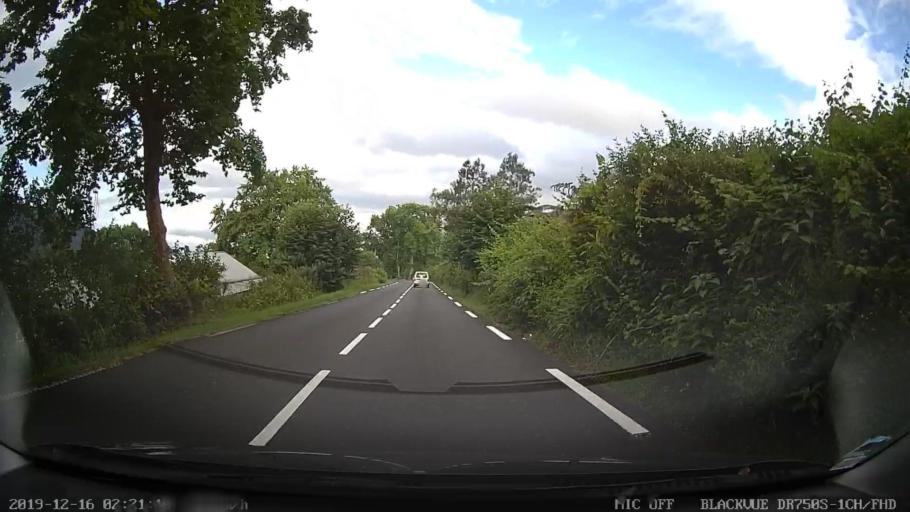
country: RE
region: Reunion
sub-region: Reunion
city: Cilaos
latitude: -21.1508
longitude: 55.6147
